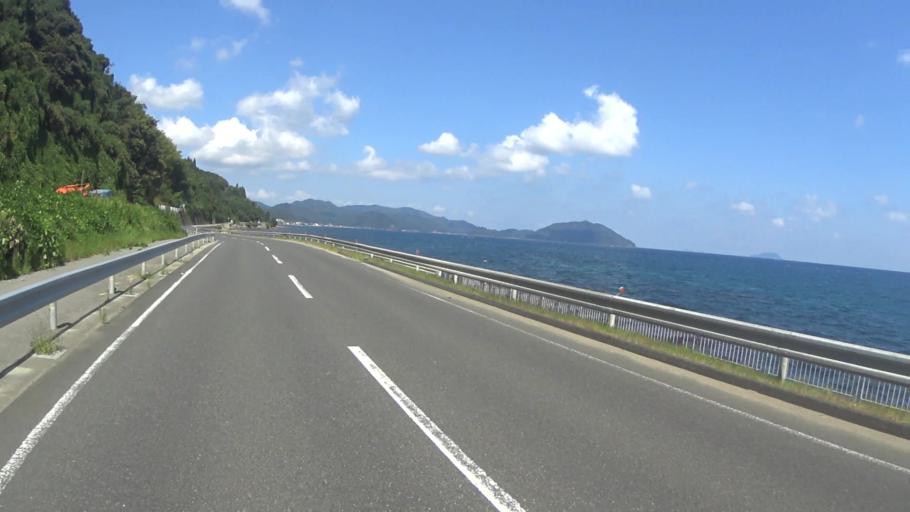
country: JP
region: Kyoto
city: Miyazu
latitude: 35.6326
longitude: 135.2469
